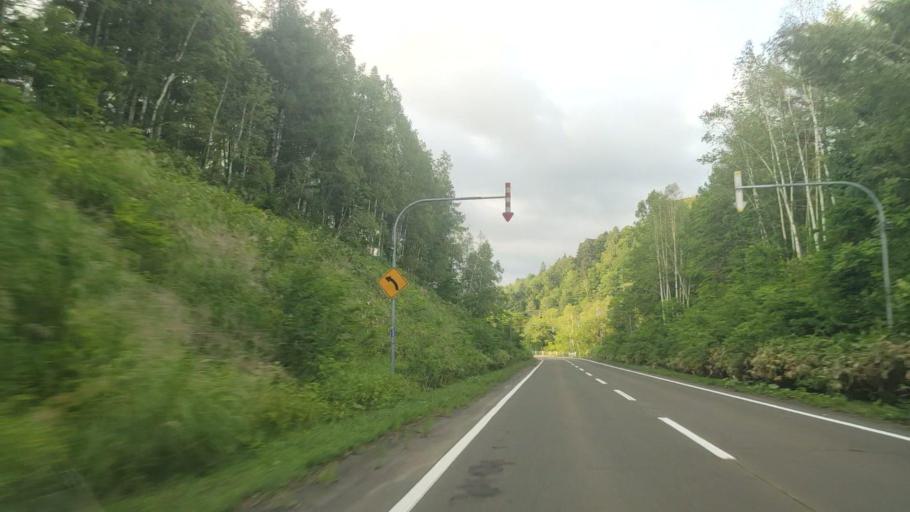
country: JP
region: Hokkaido
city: Bibai
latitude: 43.1366
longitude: 142.0961
